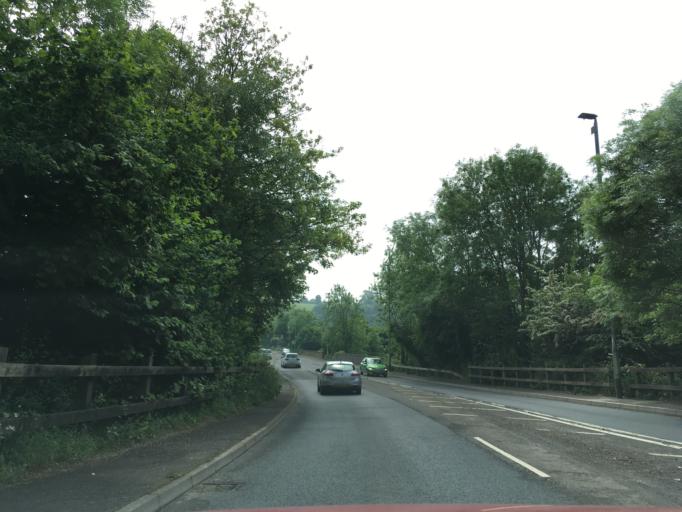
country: GB
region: England
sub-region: Devon
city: Totnes
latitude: 50.4341
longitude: -3.6933
